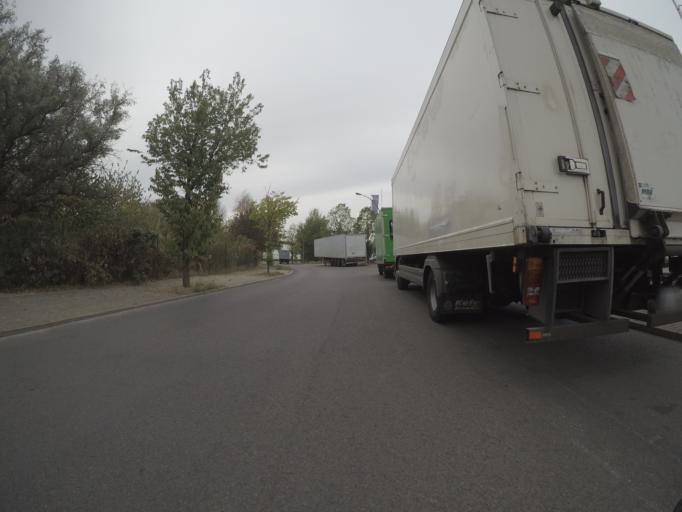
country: DE
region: Berlin
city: Alt-Hohenschoenhausen
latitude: 52.5413
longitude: 13.5260
